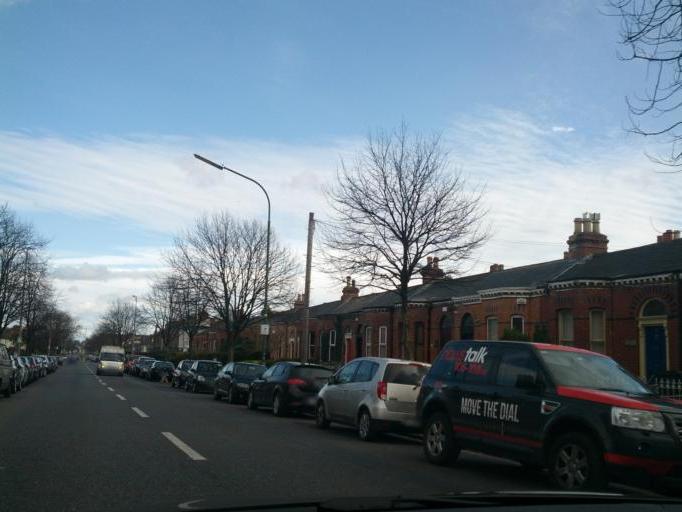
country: IE
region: Leinster
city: Drumcondra
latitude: 53.3624
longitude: -6.2504
